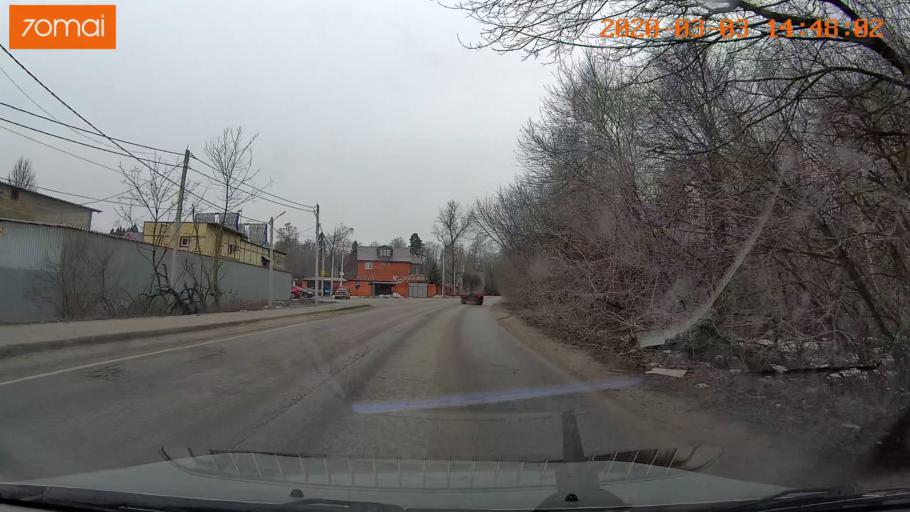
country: RU
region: Moskovskaya
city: Korenevo
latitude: 55.6886
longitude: 38.0451
